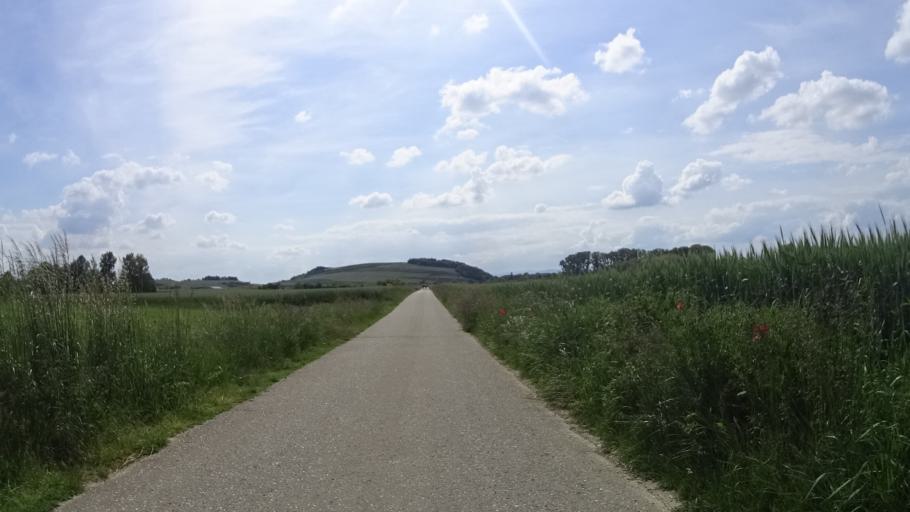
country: DE
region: Baden-Wuerttemberg
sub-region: Freiburg Region
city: Wyhl
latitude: 48.1609
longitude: 7.6306
